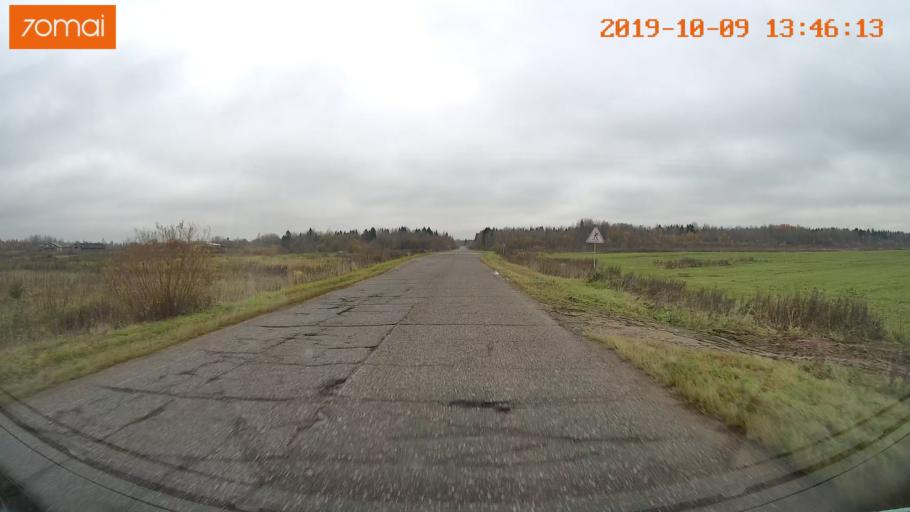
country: RU
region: Kostroma
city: Buy
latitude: 58.3817
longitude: 41.2162
